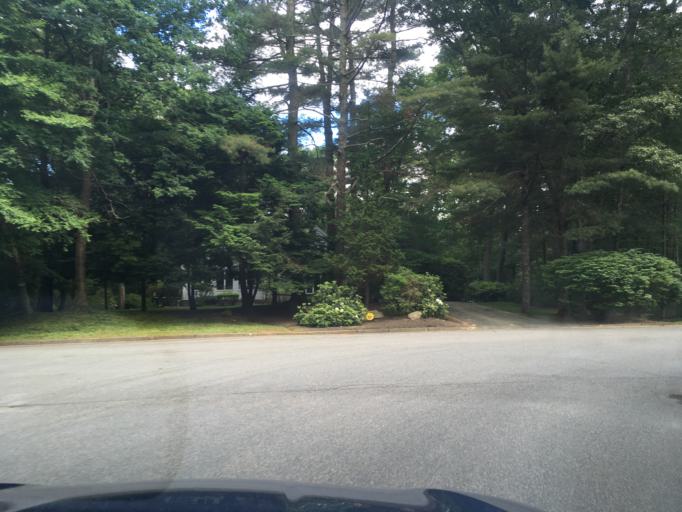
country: US
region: Rhode Island
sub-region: Washington County
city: Exeter
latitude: 41.6288
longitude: -71.5371
